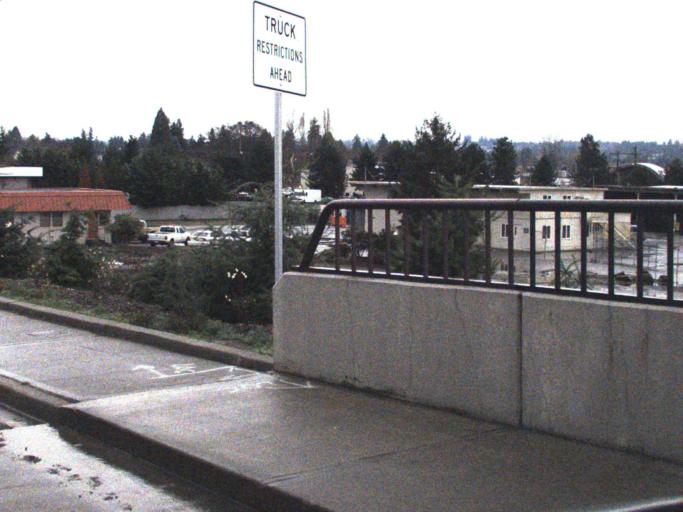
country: US
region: Washington
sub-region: Snohomish County
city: Marysville
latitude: 48.0468
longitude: -122.1778
